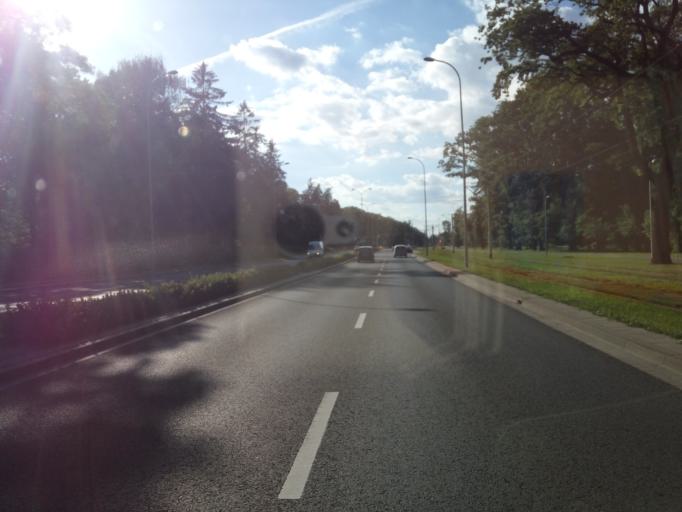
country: PL
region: Lower Silesian Voivodeship
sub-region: Powiat wroclawski
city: Wroclaw
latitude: 51.1312
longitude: 16.9760
